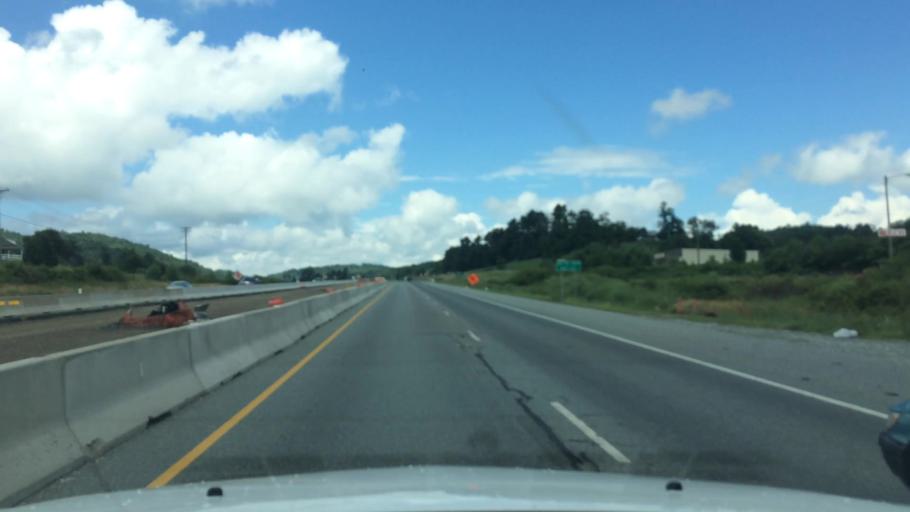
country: US
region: North Carolina
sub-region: Watauga County
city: Boone
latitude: 36.2376
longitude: -81.5124
